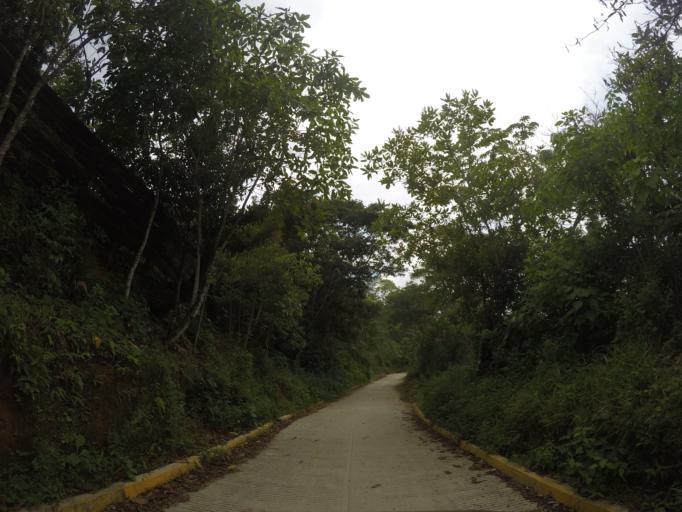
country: MX
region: Oaxaca
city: Pluma Hidalgo
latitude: 15.9174
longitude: -96.4155
